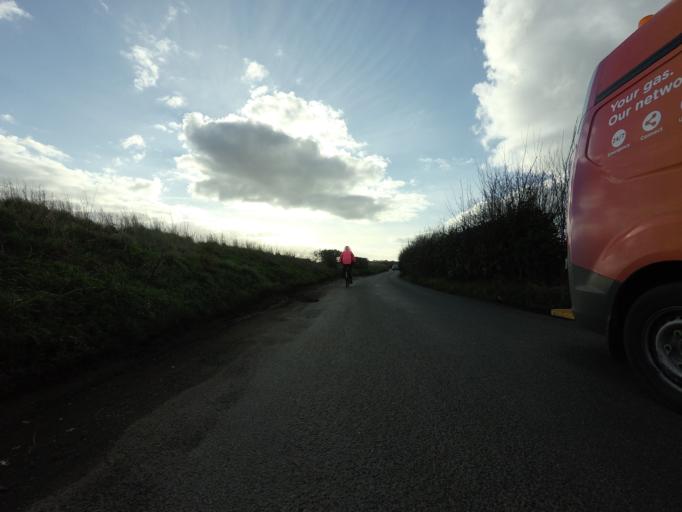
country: GB
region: England
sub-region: Kent
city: Dartford
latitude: 51.4213
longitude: 0.2084
